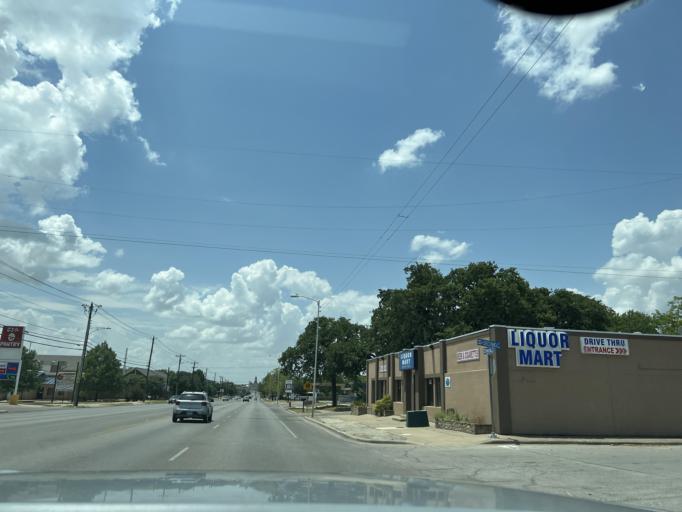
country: US
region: Texas
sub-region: Parker County
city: Weatherford
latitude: 32.7713
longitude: -97.7974
